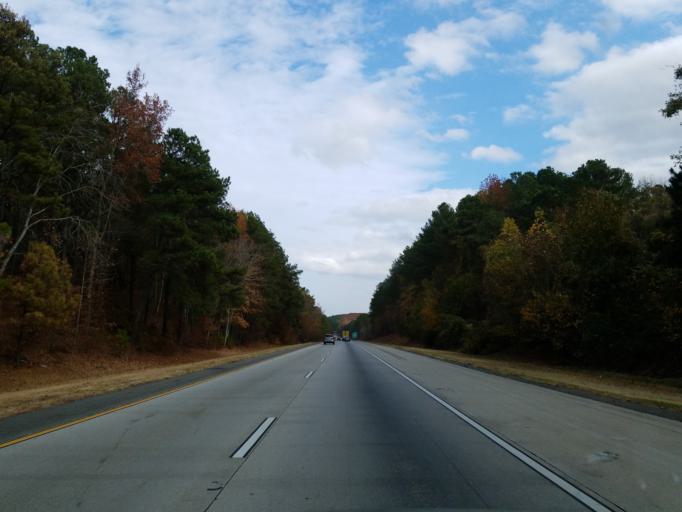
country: US
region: Georgia
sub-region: Haralson County
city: Tallapoosa
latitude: 33.6815
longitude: -85.2890
